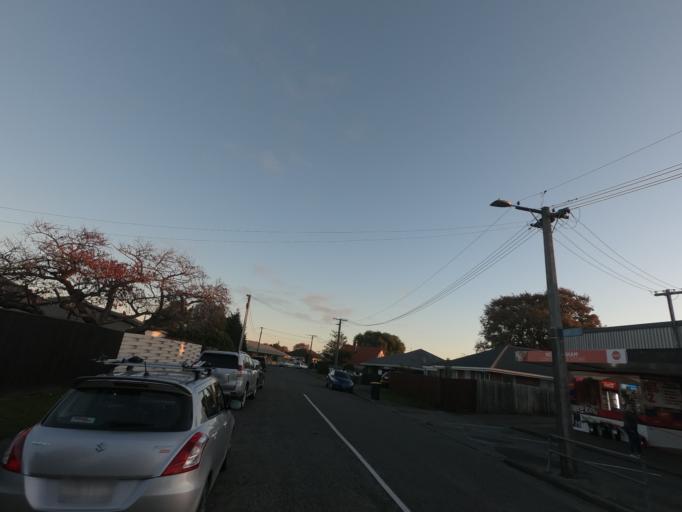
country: NZ
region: Canterbury
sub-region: Selwyn District
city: Prebbleton
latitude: -43.5754
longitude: 172.5607
